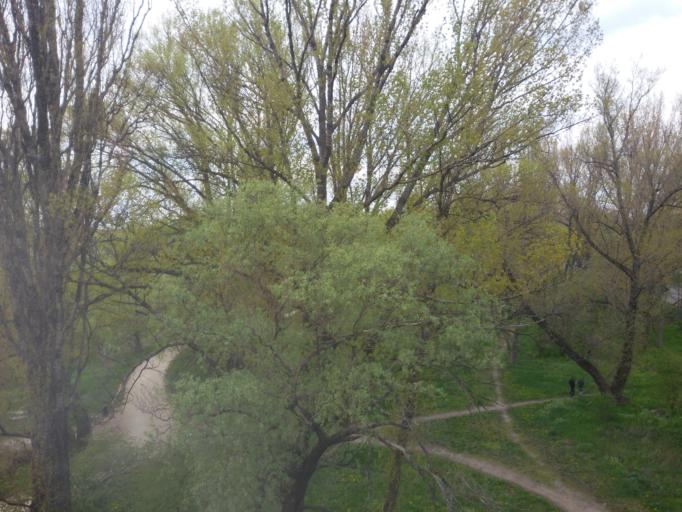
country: PL
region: Masovian Voivodeship
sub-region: Warszawa
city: Praga Polnoc
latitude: 52.2504
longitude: 21.0242
